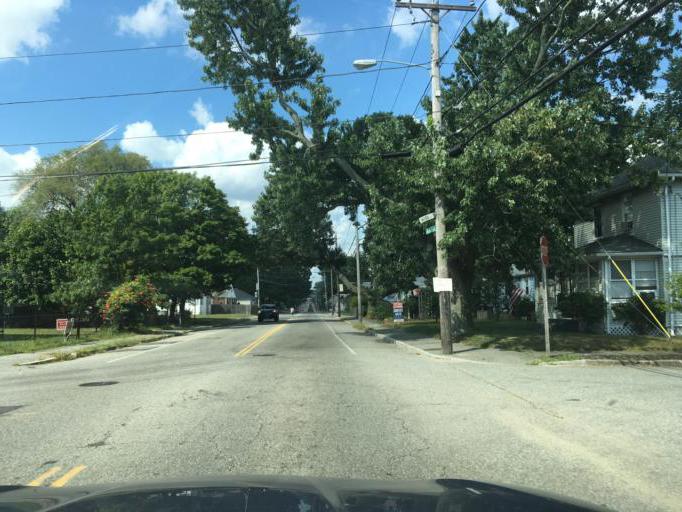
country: US
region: Rhode Island
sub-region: Kent County
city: Warwick
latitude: 41.6937
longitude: -71.3984
